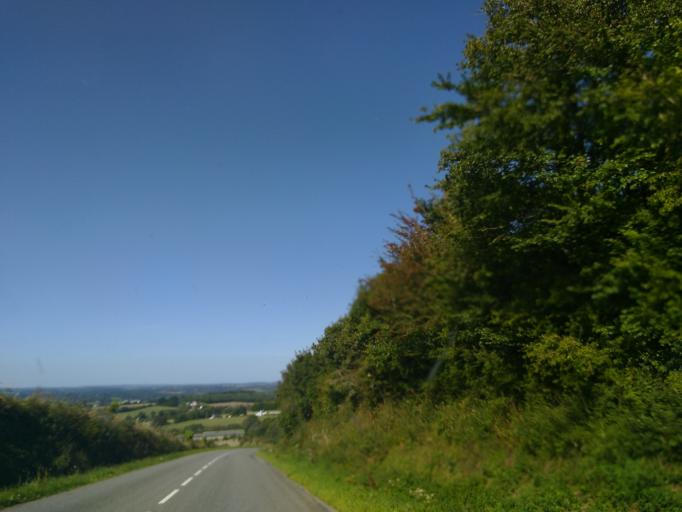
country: FR
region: Brittany
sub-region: Departement du Finistere
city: Le Faou
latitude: 48.2656
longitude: -4.1939
